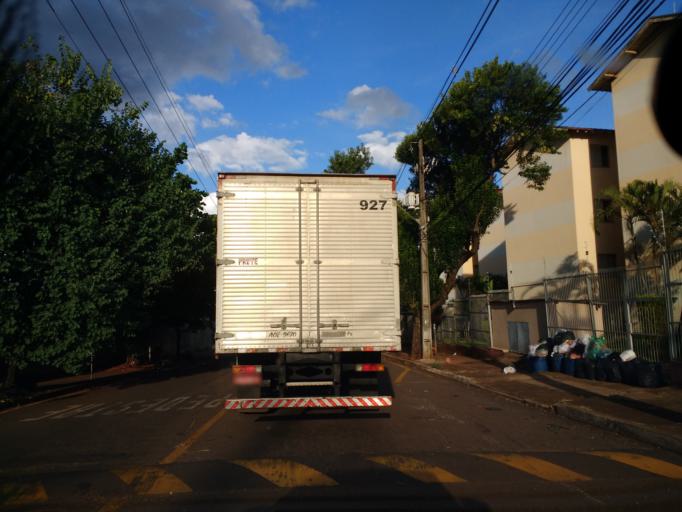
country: BR
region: Parana
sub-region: Londrina
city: Londrina
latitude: -23.2953
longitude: -51.1680
